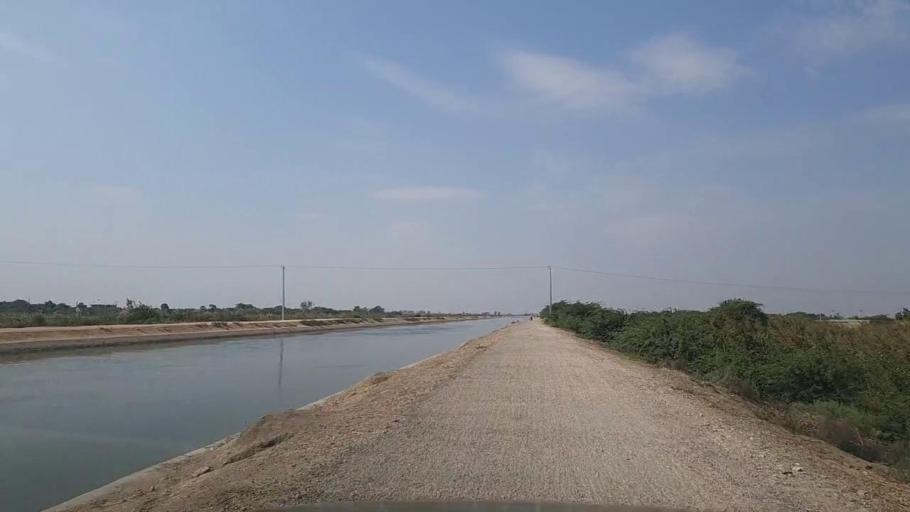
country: PK
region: Sindh
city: Thatta
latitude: 24.7532
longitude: 67.7670
